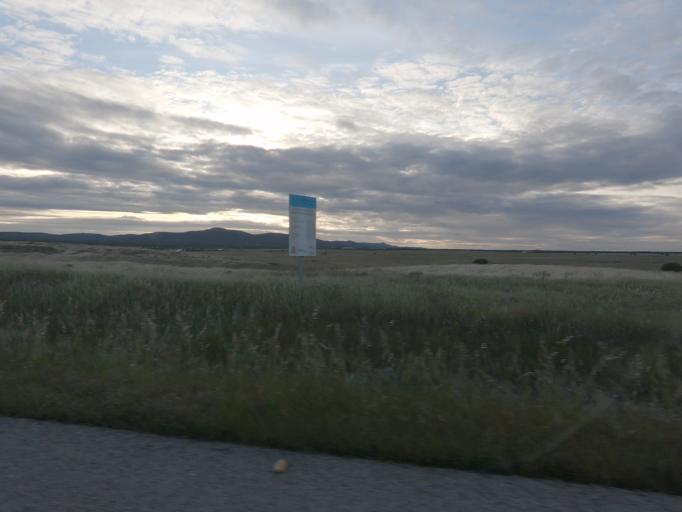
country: ES
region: Extremadura
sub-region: Provincia de Caceres
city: Malpartida de Caceres
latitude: 39.3478
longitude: -6.4712
